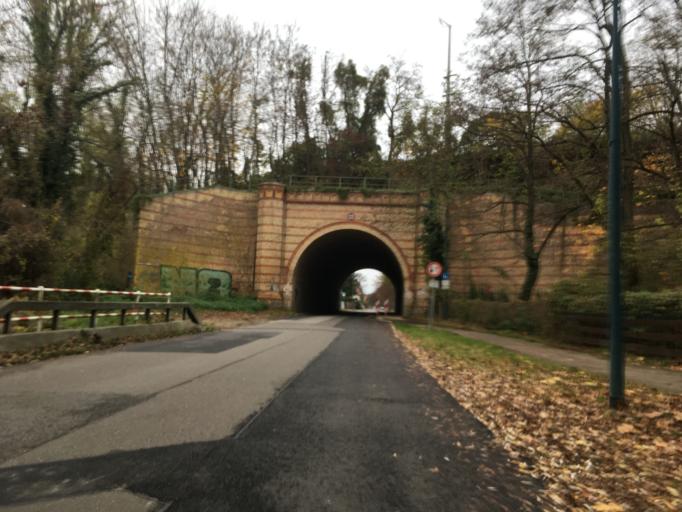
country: DE
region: Brandenburg
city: Frankfurt (Oder)
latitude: 52.3167
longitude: 14.5540
